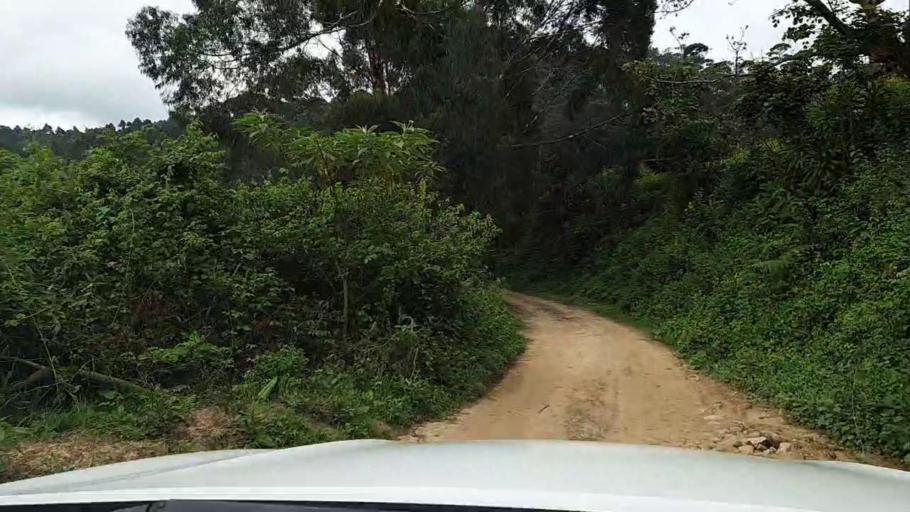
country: RW
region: Western Province
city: Kibuye
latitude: -2.2744
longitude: 29.3639
